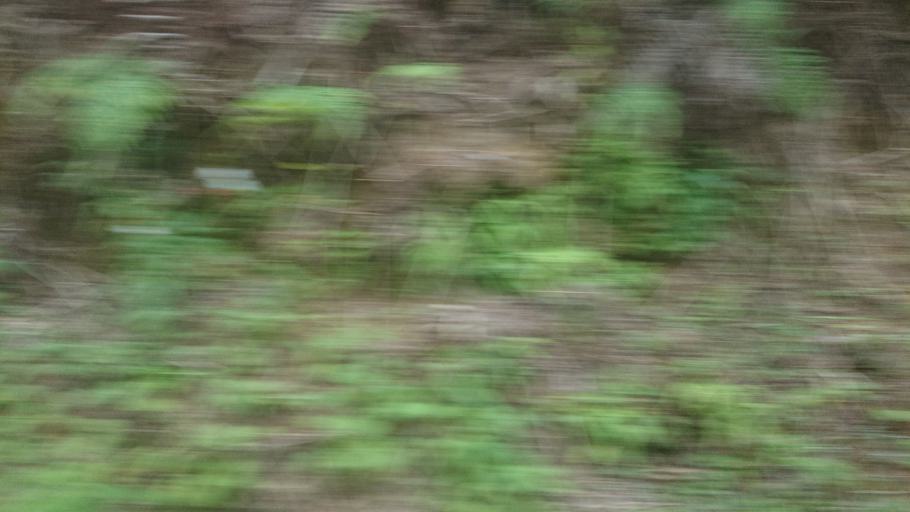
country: TW
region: Taiwan
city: Lugu
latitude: 23.6217
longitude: 120.7202
